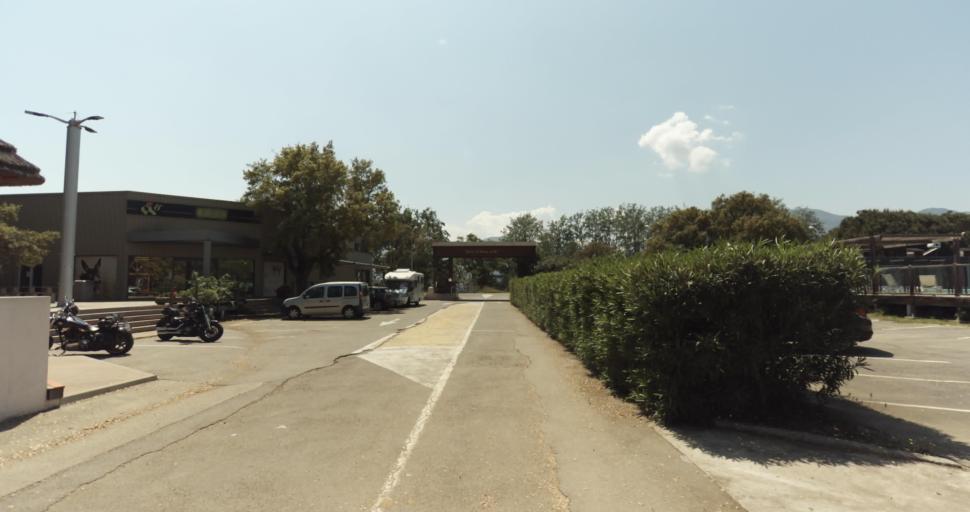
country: FR
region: Corsica
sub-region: Departement de la Haute-Corse
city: Biguglia
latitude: 42.6292
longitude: 9.4678
